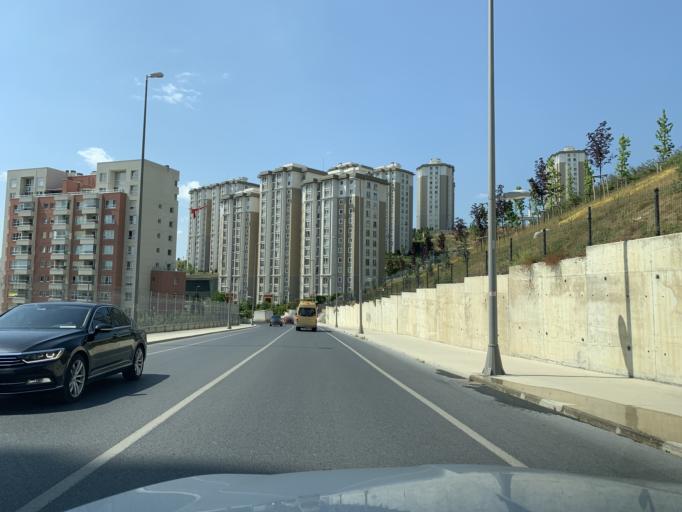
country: TR
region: Istanbul
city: Esenyurt
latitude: 41.0784
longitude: 28.6933
